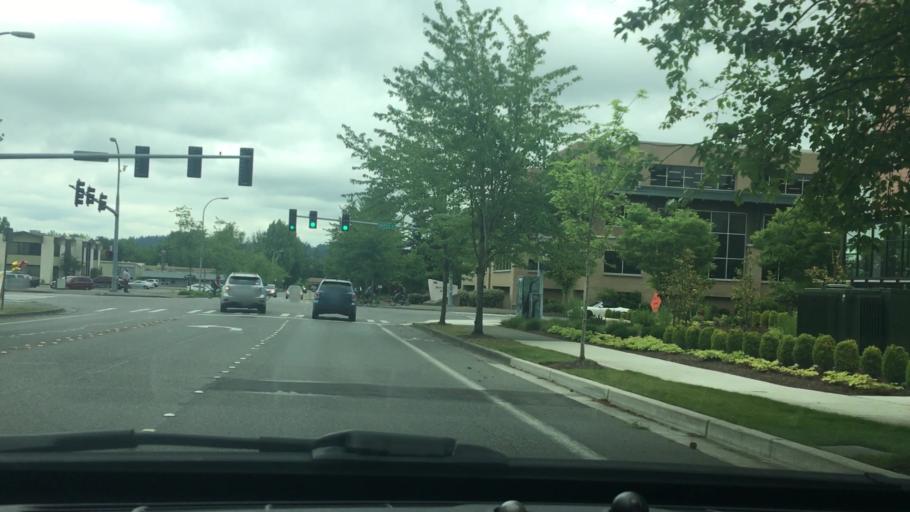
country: US
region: Washington
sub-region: King County
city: Issaquah
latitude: 47.5425
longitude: -122.0575
